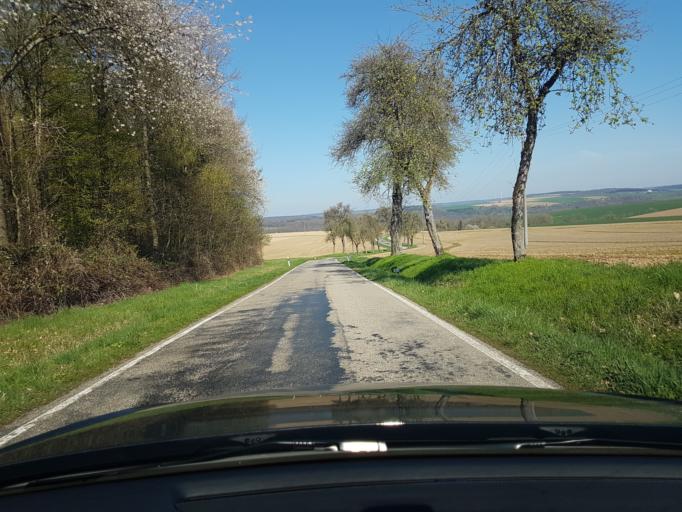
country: DE
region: Baden-Wuerttemberg
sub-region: Regierungsbezirk Stuttgart
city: Jagsthausen
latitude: 49.3168
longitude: 9.5148
